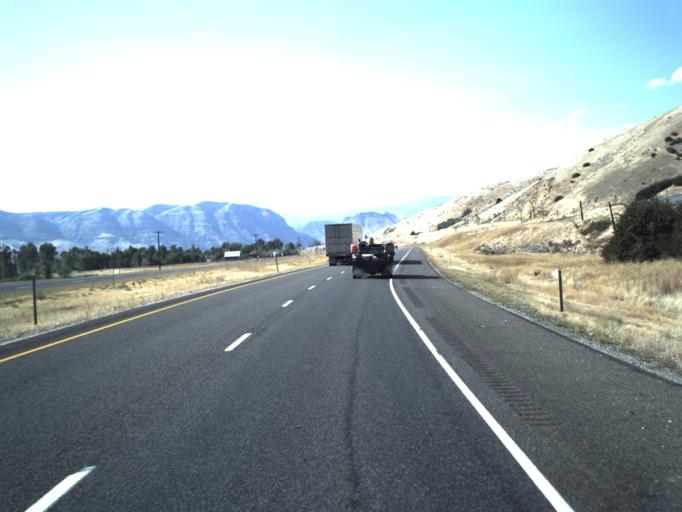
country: US
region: Utah
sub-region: Summit County
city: Coalville
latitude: 40.9956
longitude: -111.4635
